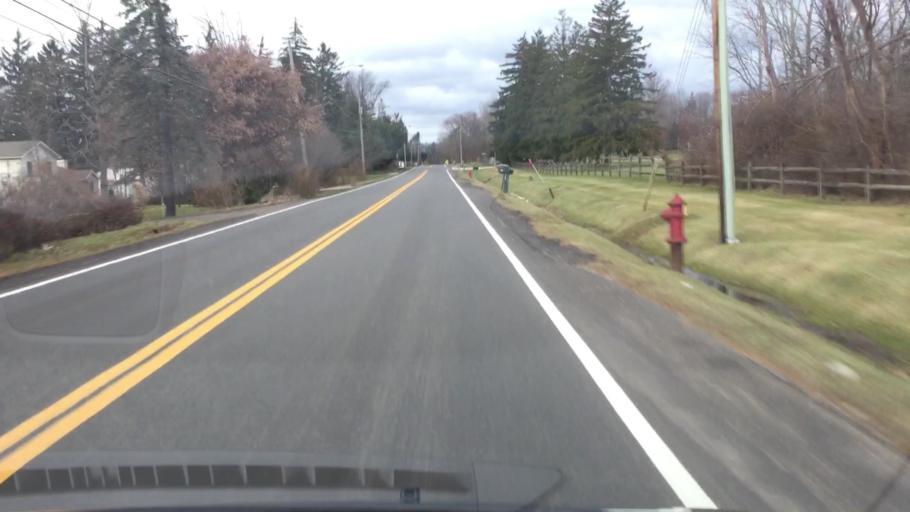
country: US
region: Ohio
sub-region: Summit County
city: Boston Heights
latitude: 41.2712
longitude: -81.5135
